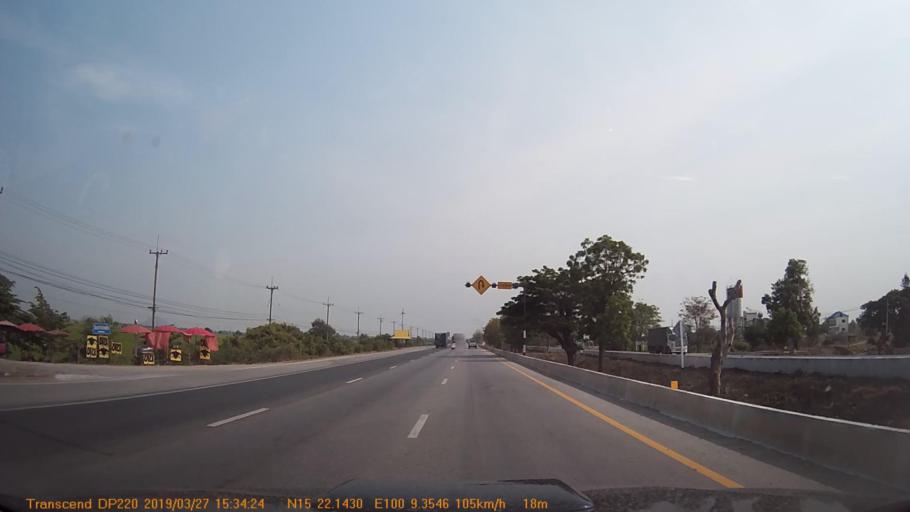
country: TH
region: Nakhon Sawan
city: Phayuha Khiri
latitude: 15.3687
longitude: 100.1560
